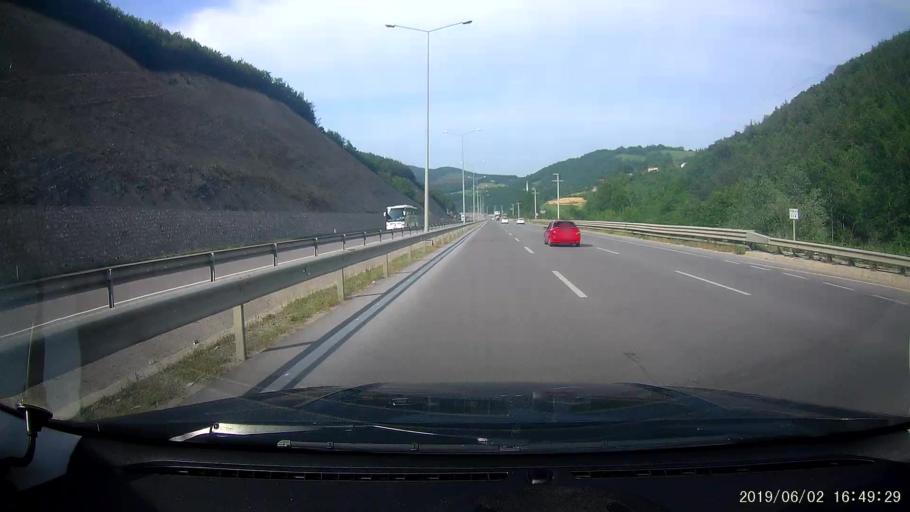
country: TR
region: Samsun
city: Samsun
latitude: 41.2382
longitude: 36.1627
